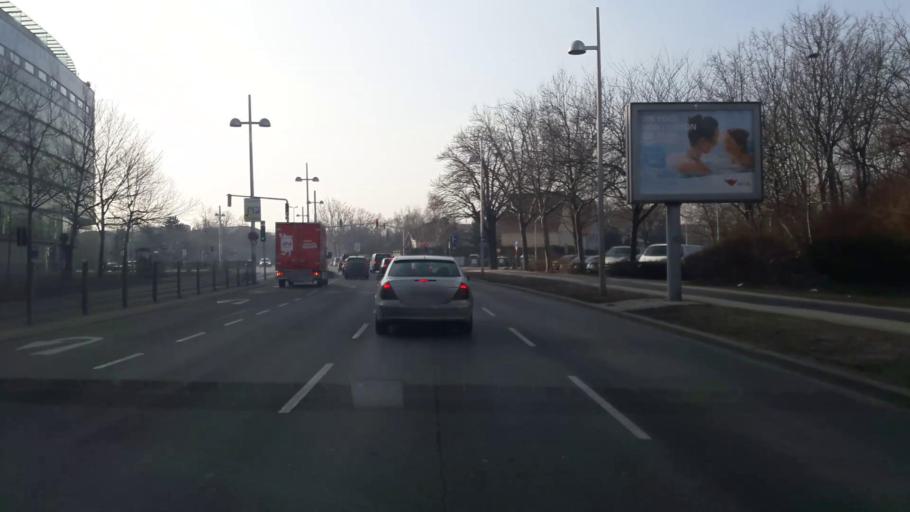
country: AT
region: Lower Austria
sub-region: Politischer Bezirk Modling
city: Vosendorf
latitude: 48.1496
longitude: 16.3110
